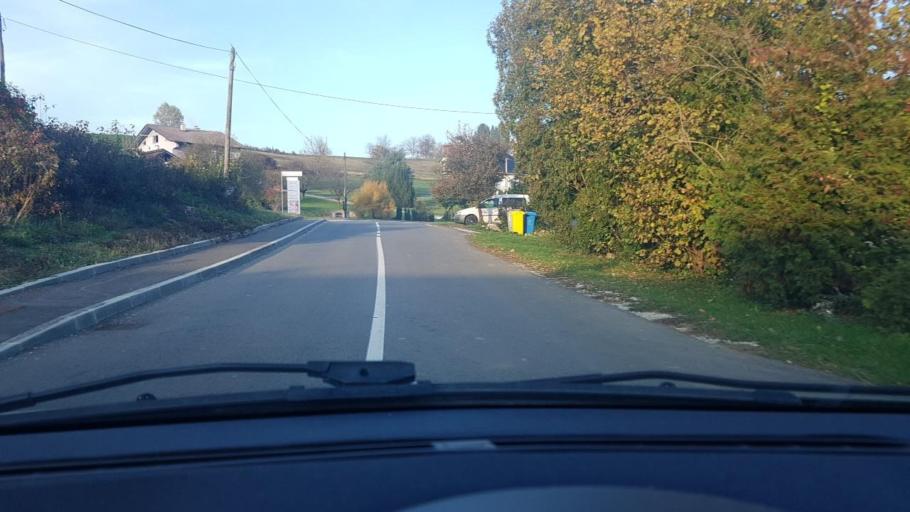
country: SI
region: Rogaska Slatina
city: Rogaska Slatina
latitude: 46.2123
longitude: 15.6525
